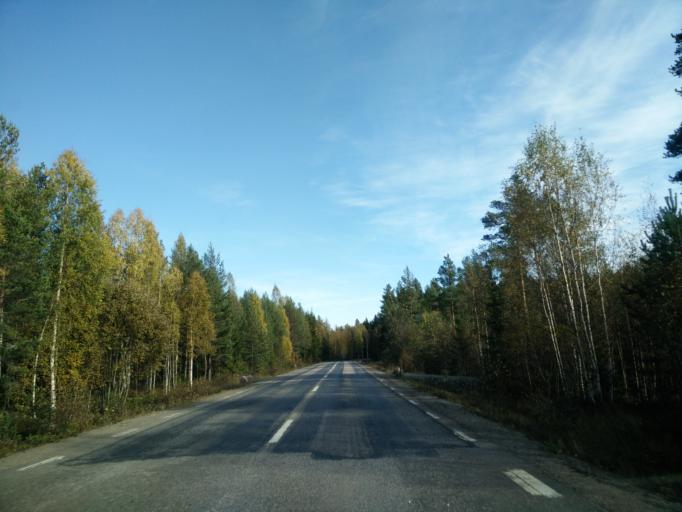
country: SE
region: Gaevleborg
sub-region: Hudiksvalls Kommun
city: Iggesund
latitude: 61.5519
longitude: 16.9849
